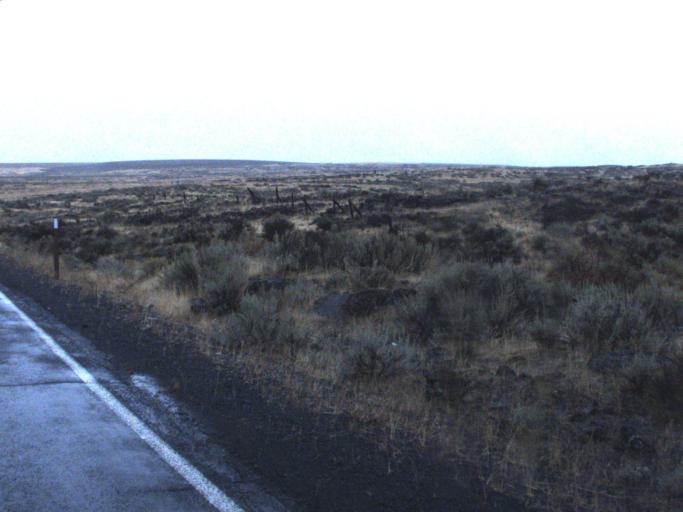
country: US
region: Washington
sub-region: Lincoln County
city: Davenport
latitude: 47.3678
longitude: -118.1133
